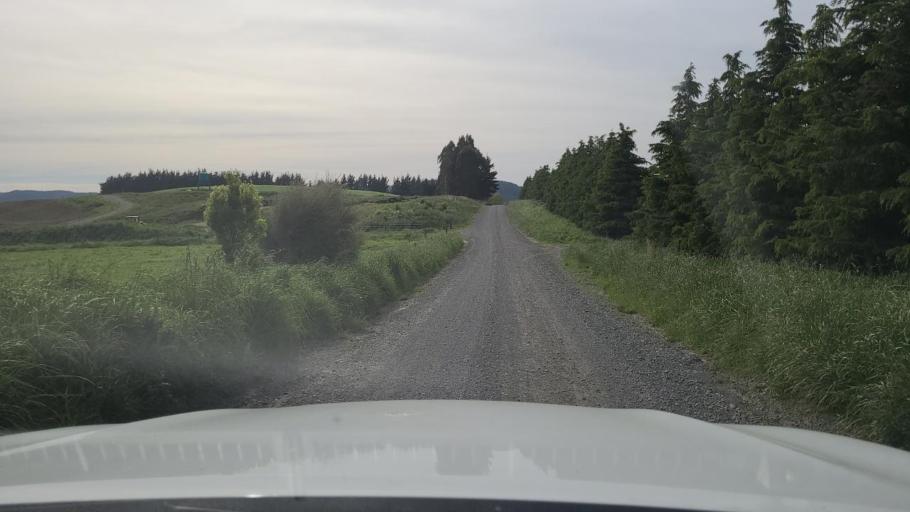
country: NZ
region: Hawke's Bay
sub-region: Napier City
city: Taradale
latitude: -39.3009
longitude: 176.6424
